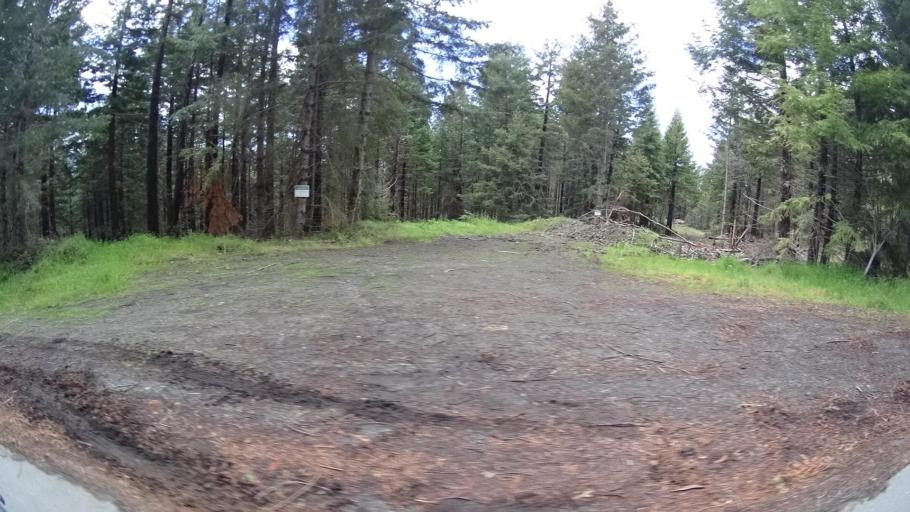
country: US
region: California
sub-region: Humboldt County
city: Blue Lake
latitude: 40.8584
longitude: -123.9347
